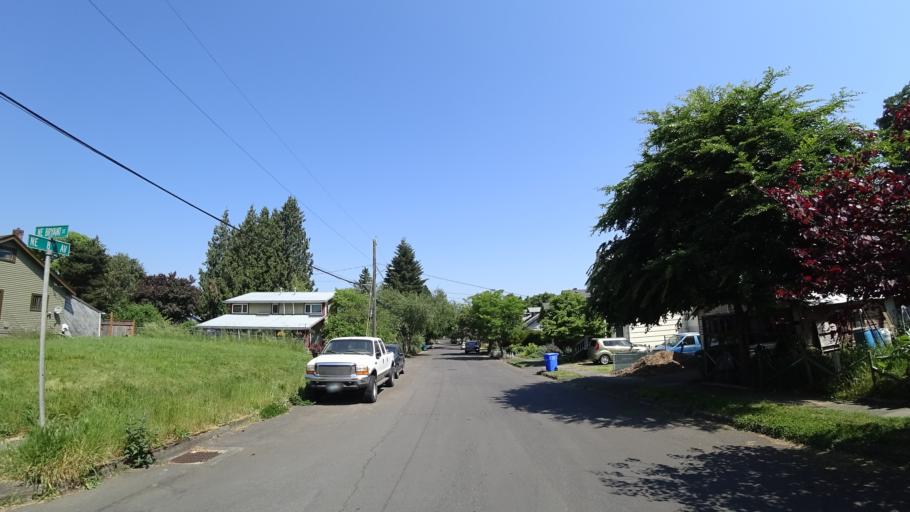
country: US
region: Oregon
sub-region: Multnomah County
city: Portland
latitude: 45.5732
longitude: -122.6566
